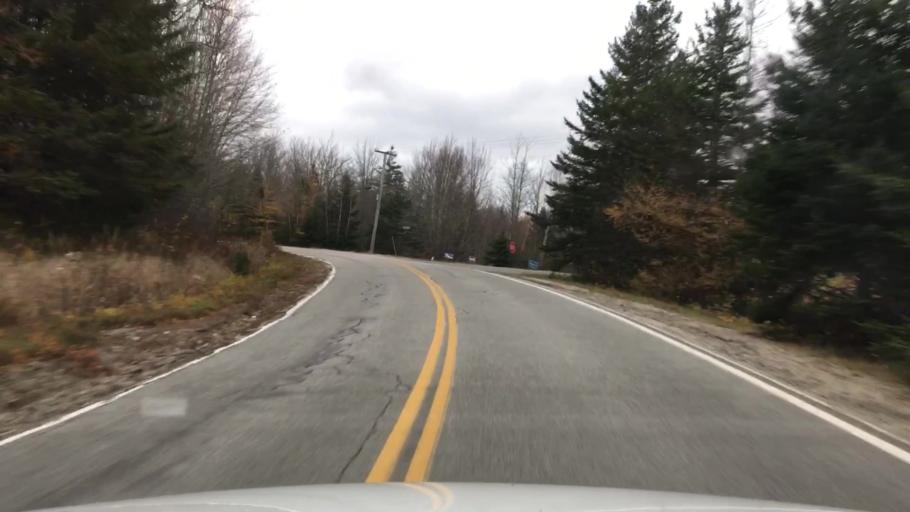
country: US
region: Maine
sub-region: Hancock County
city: Sedgwick
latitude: 44.2772
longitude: -68.5543
